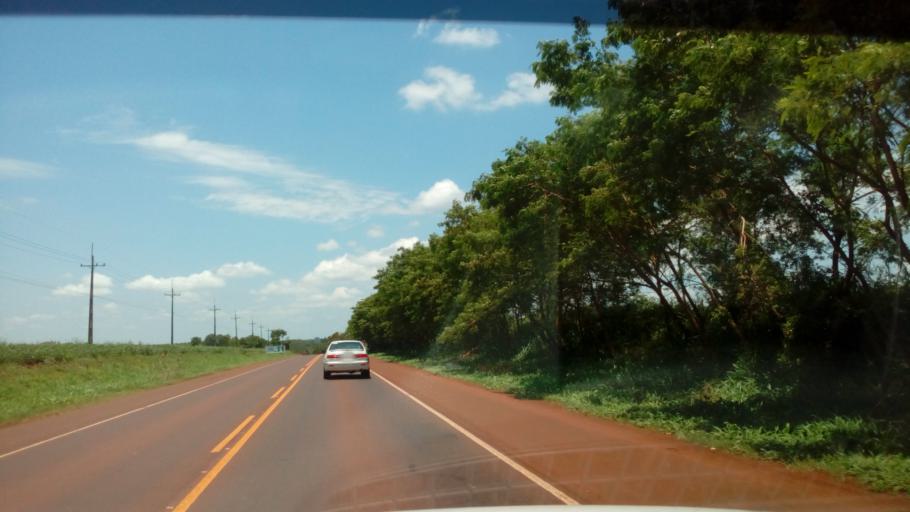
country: PY
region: Alto Parana
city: Naranjal
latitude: -25.9461
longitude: -55.1219
